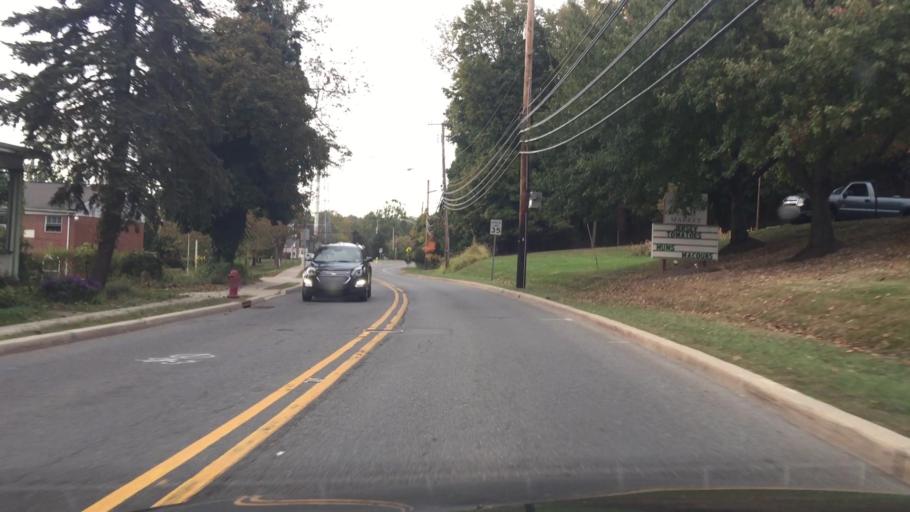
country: US
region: New Jersey
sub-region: Hunterdon County
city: Lambertville
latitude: 40.3758
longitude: -74.9457
